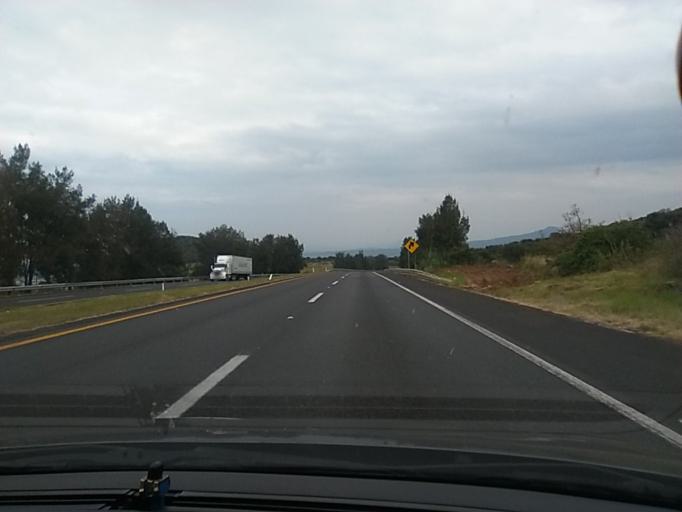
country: MX
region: Michoacan
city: Penjamillo de Degollado
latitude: 20.0815
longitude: -101.9855
